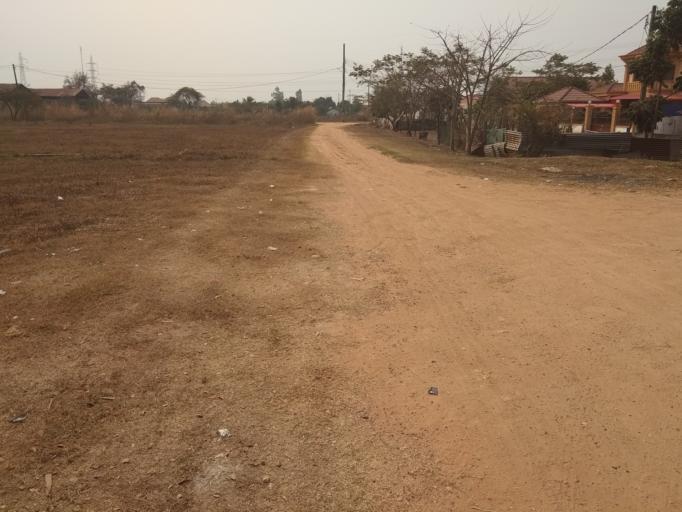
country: LA
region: Vientiane
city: Vientiane
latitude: 17.9621
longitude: 102.6693
